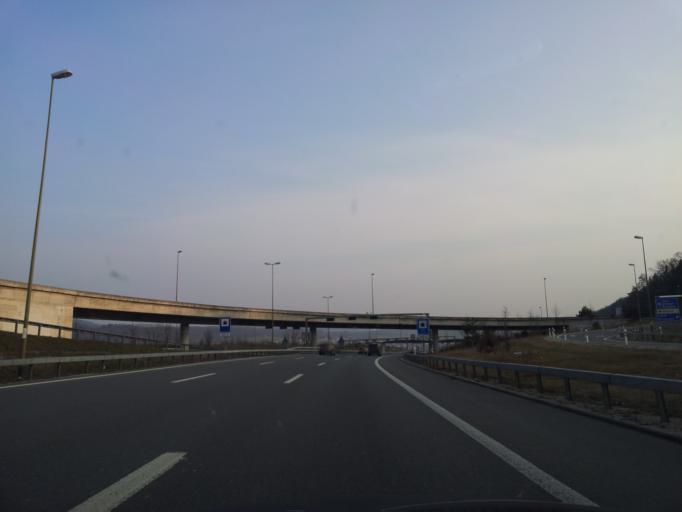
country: CH
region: Zurich
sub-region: Bezirk Affoltern
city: Wettswil / Wettswil (Dorf)
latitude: 47.3395
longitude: 8.4589
